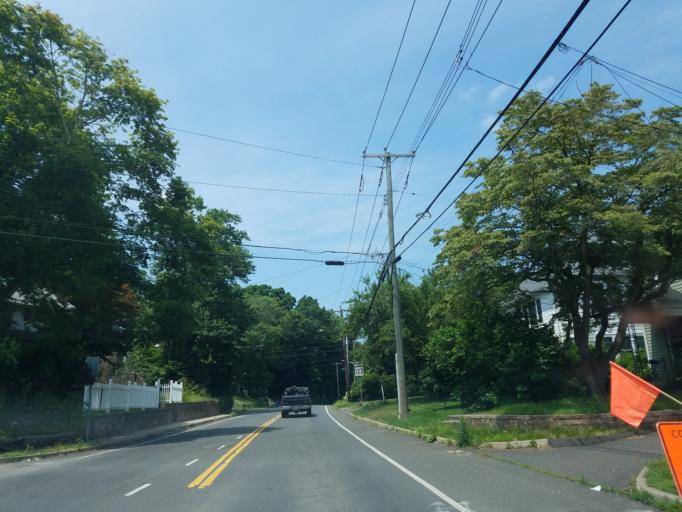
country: US
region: Connecticut
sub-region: New Haven County
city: New Haven
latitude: 41.3082
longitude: -72.9697
